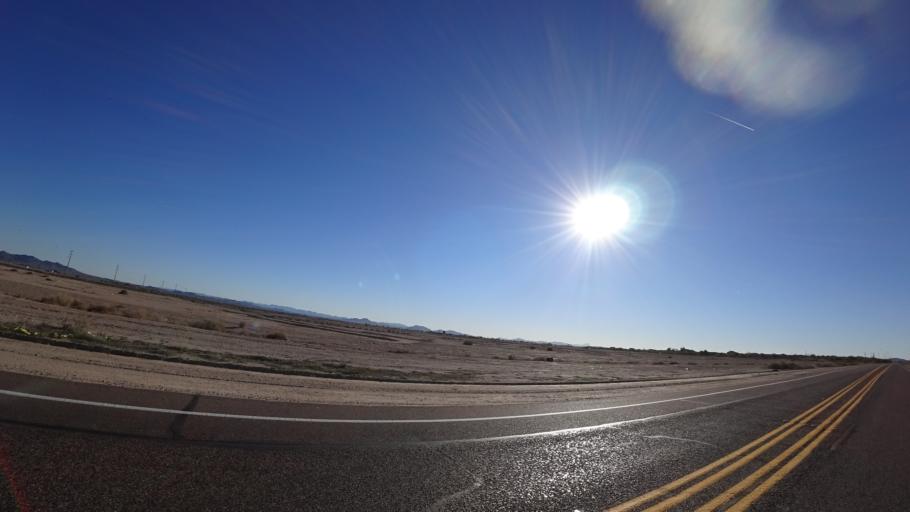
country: US
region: Arizona
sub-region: Maricopa County
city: Citrus Park
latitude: 33.4502
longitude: -112.4648
